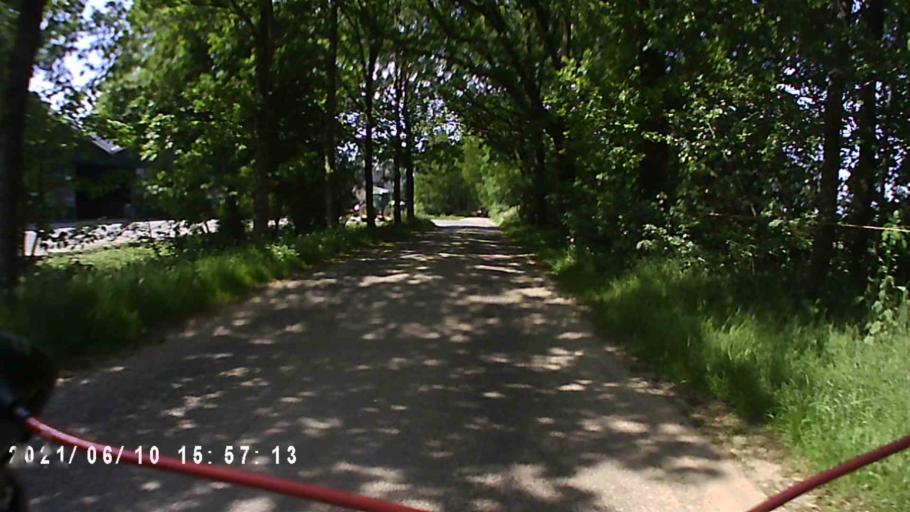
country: NL
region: Friesland
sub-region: Gemeente Achtkarspelen
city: Drogeham
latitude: 53.1884
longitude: 6.0960
